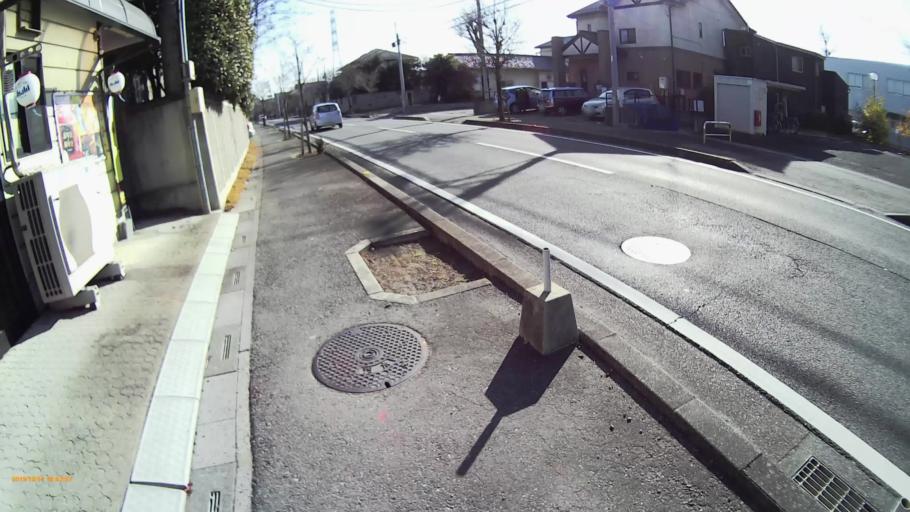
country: JP
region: Saitama
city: Fukayacho
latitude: 36.1768
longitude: 139.3380
